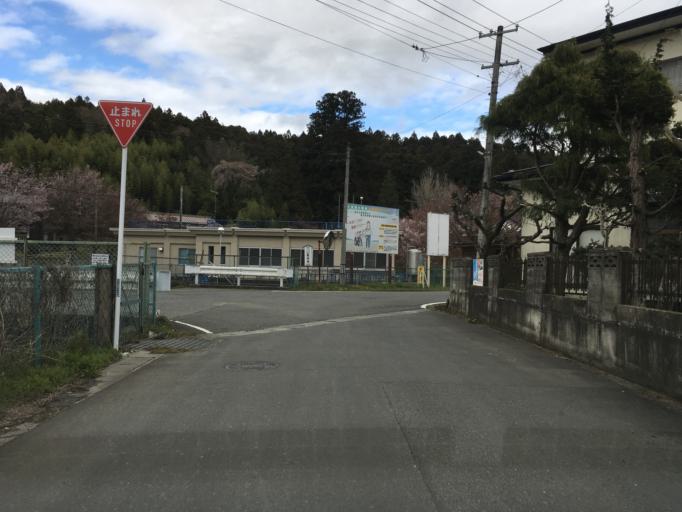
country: JP
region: Iwate
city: Ichinoseki
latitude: 38.7628
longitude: 141.2684
